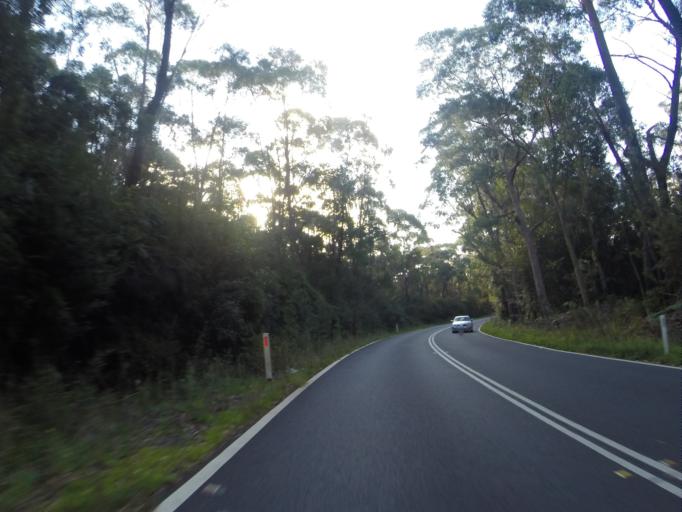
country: AU
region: New South Wales
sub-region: Shoalhaven Shire
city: Kangaroo Valley
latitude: -34.6863
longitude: 150.4919
